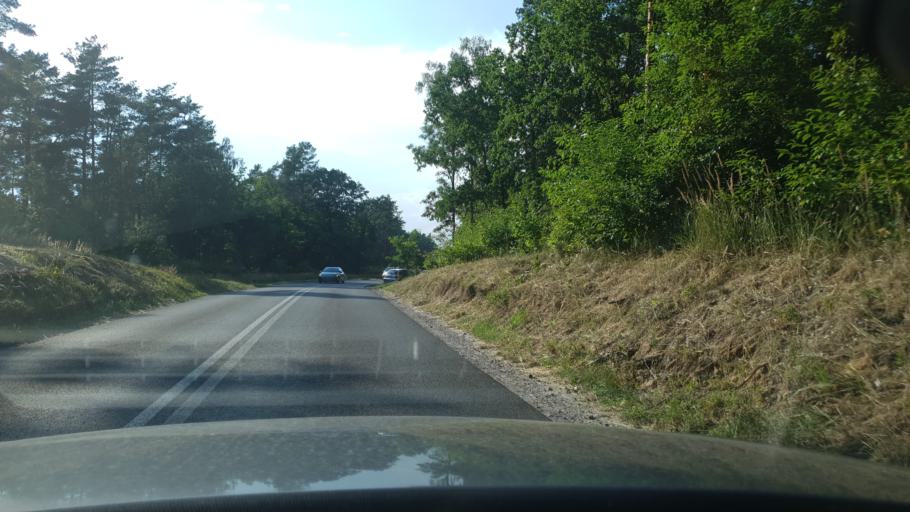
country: PL
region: Kujawsko-Pomorskie
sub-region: Grudziadz
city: Grudziadz
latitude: 53.4455
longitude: 18.7450
